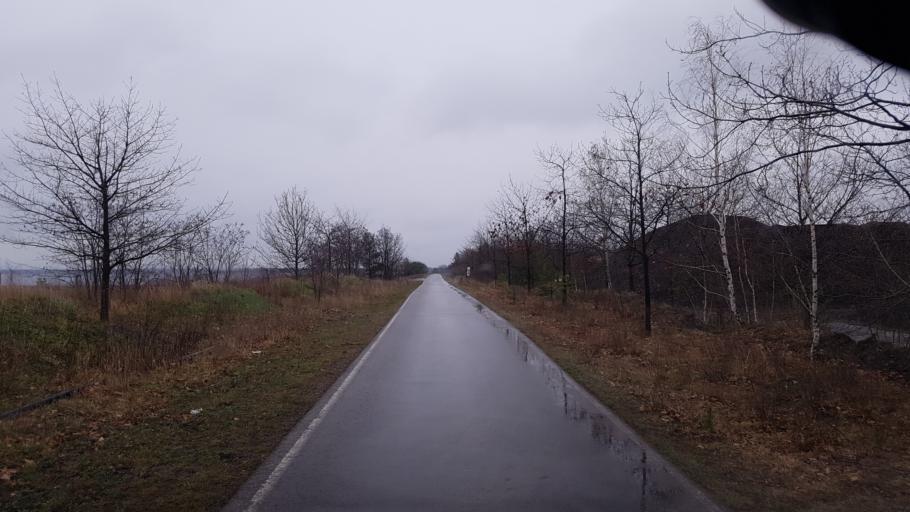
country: DE
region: Brandenburg
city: Grossraschen
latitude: 51.5756
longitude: 13.9824
